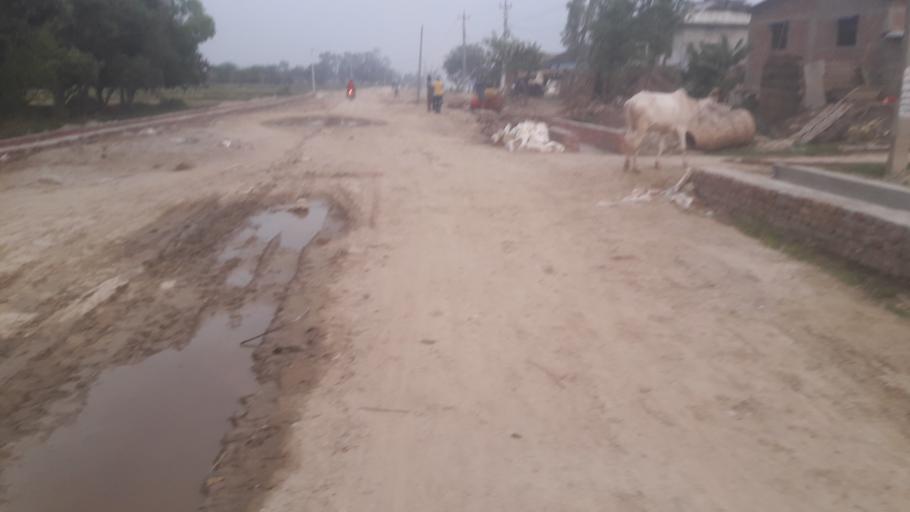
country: NP
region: Eastern Region
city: Siraha
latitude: 26.6564
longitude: 86.1959
